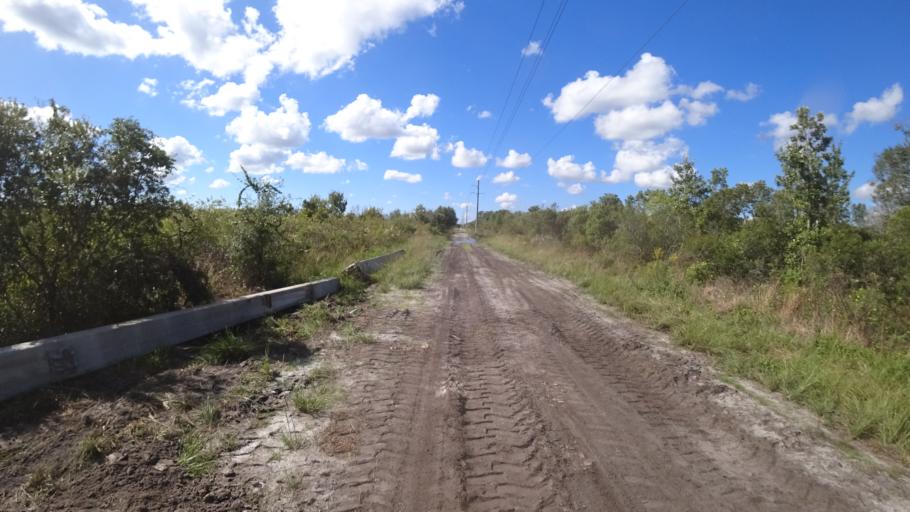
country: US
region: Florida
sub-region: Sarasota County
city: Lake Sarasota
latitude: 27.2460
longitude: -82.2772
